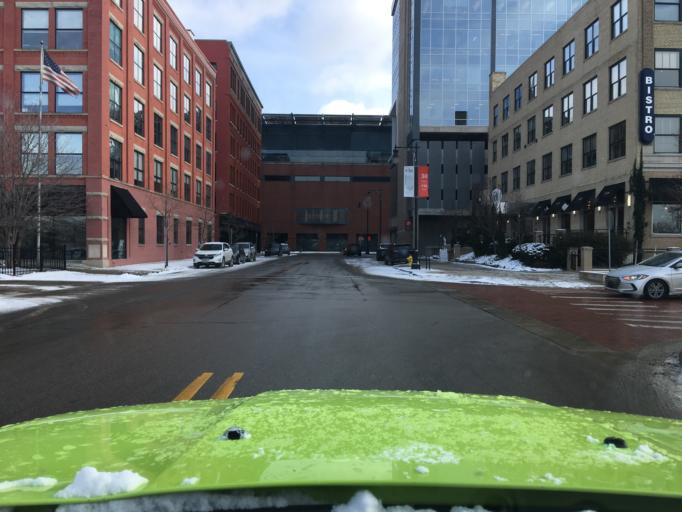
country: US
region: Michigan
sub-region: Kent County
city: Grand Rapids
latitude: 42.9621
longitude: -85.6732
